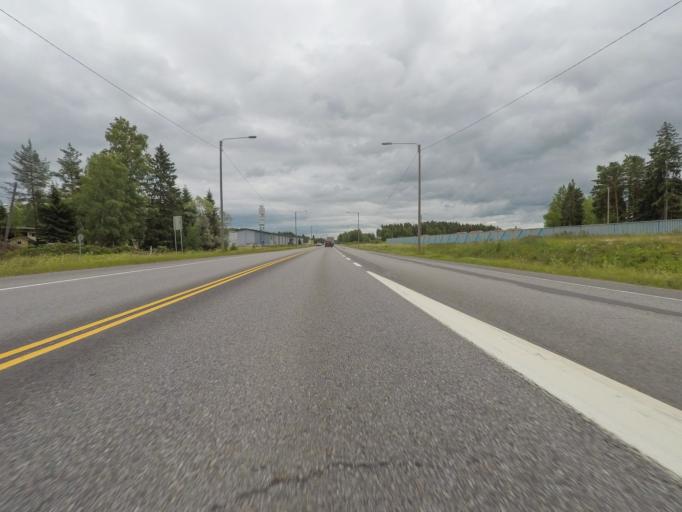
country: FI
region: Varsinais-Suomi
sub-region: Turku
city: Lieto
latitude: 60.4629
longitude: 22.4207
